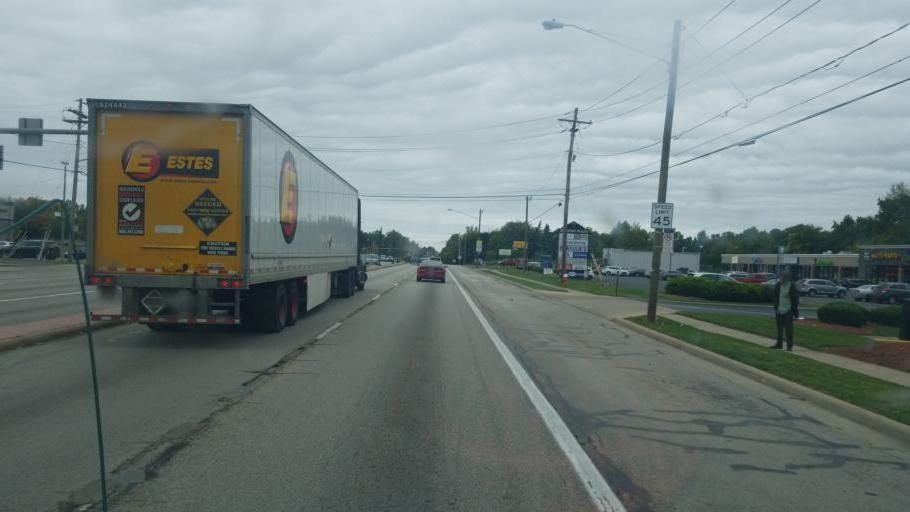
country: US
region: Ohio
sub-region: Lucas County
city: Maumee
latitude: 41.6052
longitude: -83.6646
